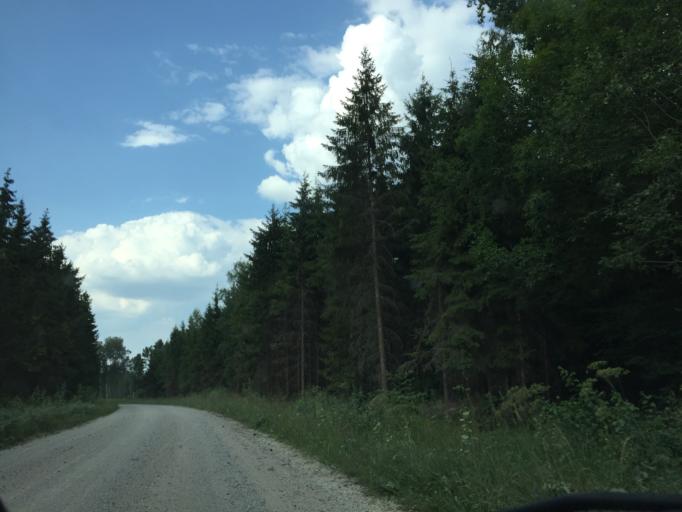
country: LV
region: Auces Novads
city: Auce
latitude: 56.4117
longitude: 22.9929
